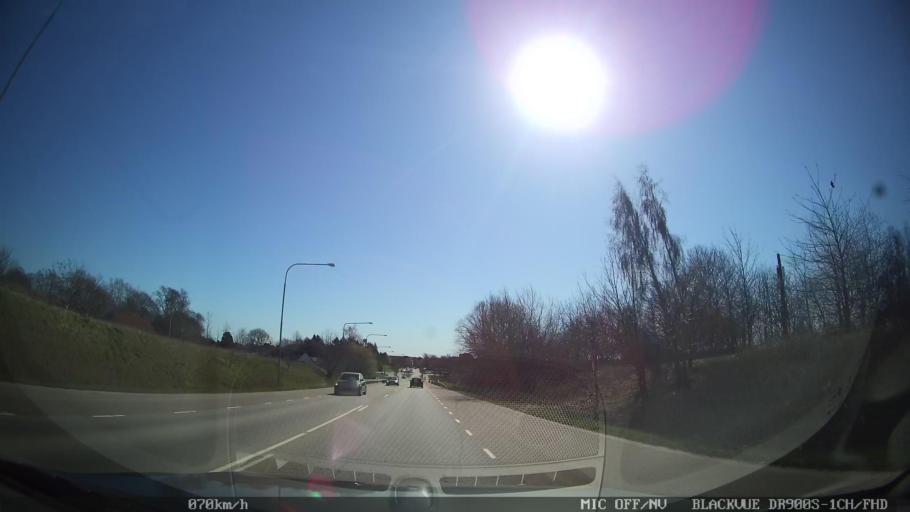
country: SE
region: Skane
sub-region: Ystads Kommun
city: Ystad
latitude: 55.4350
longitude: 13.7982
